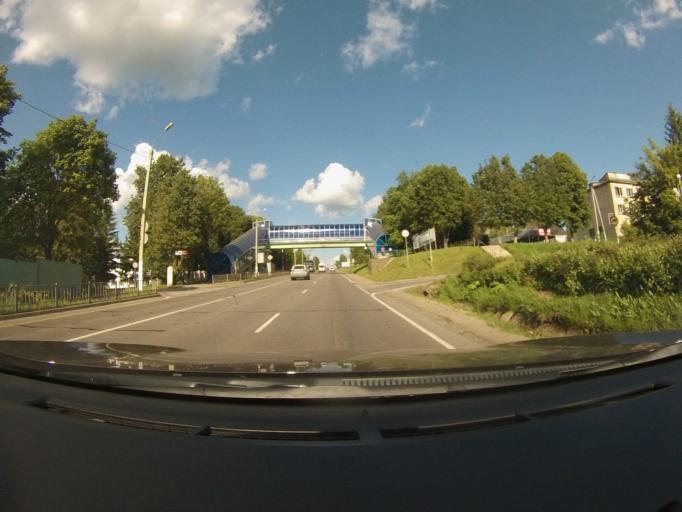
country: RU
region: Tula
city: Chern'
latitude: 53.4544
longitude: 36.9090
